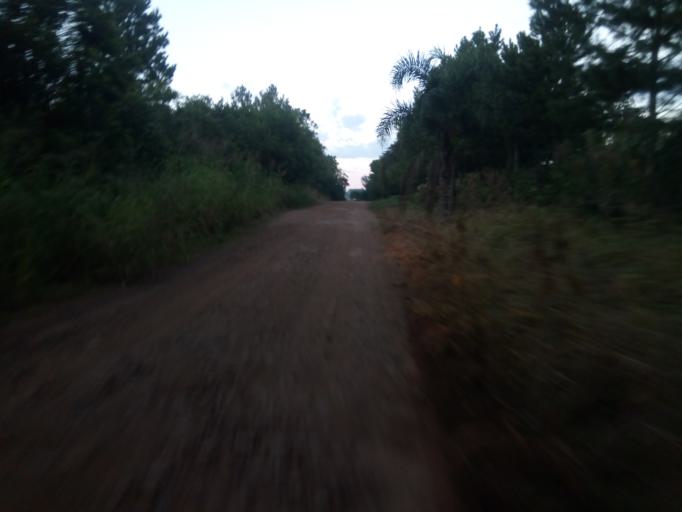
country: AR
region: Misiones
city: Almafuerte
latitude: -27.5648
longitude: -55.4116
